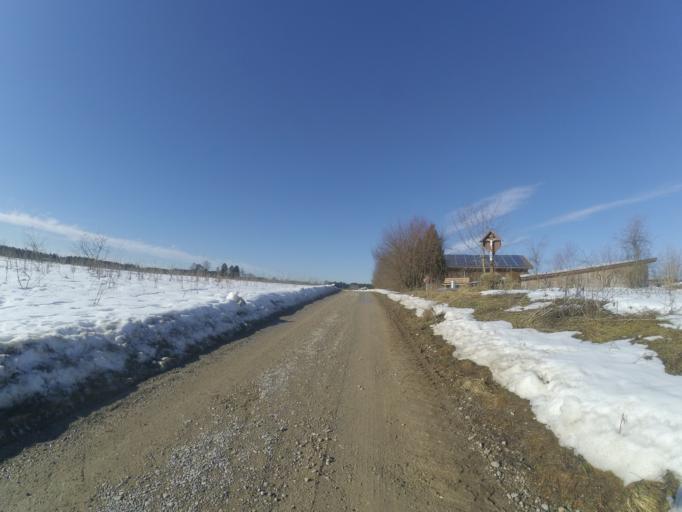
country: DE
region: Bavaria
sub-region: Upper Bavaria
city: Aying
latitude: 47.9769
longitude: 11.7668
